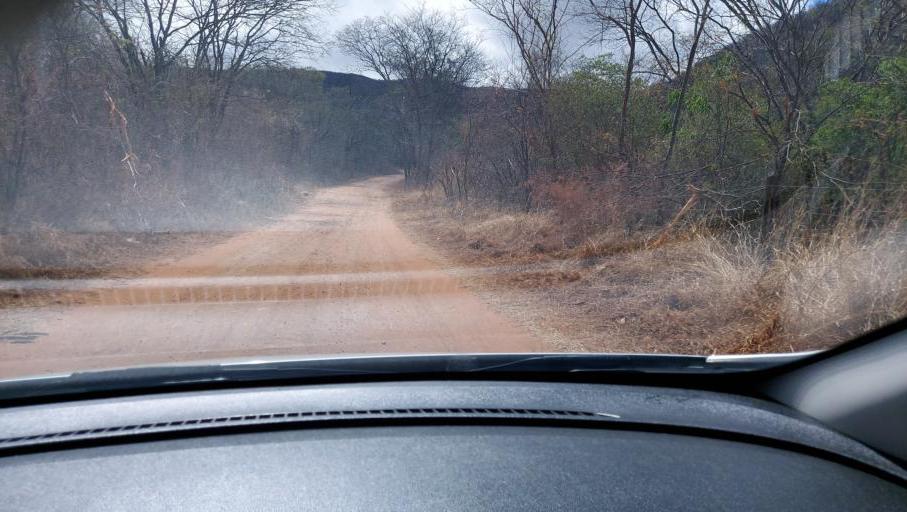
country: BR
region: Bahia
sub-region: Oliveira Dos Brejinhos
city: Beira Rio
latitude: -12.0975
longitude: -42.5489
